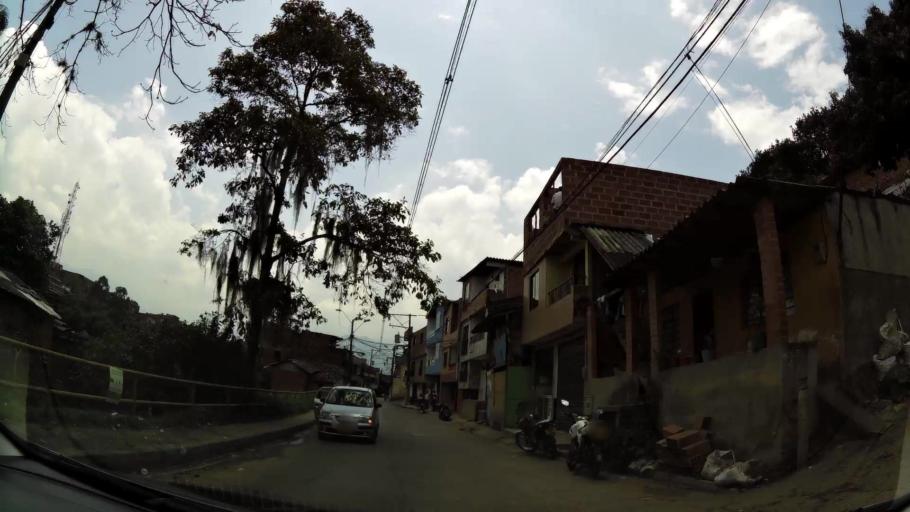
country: CO
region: Antioquia
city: Itagui
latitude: 6.1810
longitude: -75.6127
